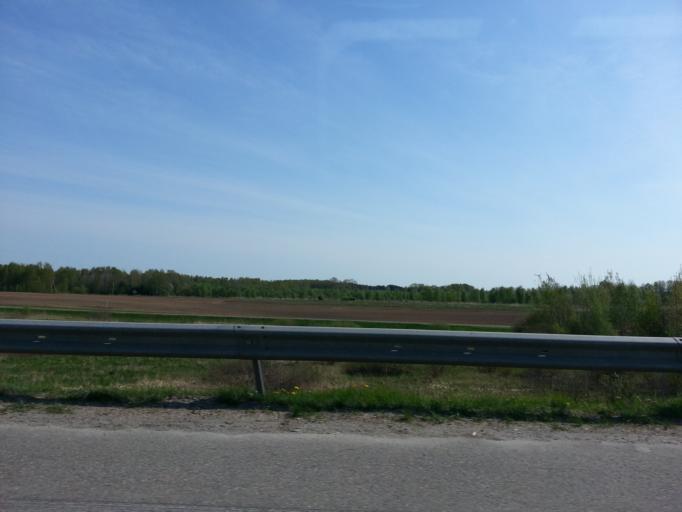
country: LT
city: Sirvintos
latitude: 54.8900
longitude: 25.0564
